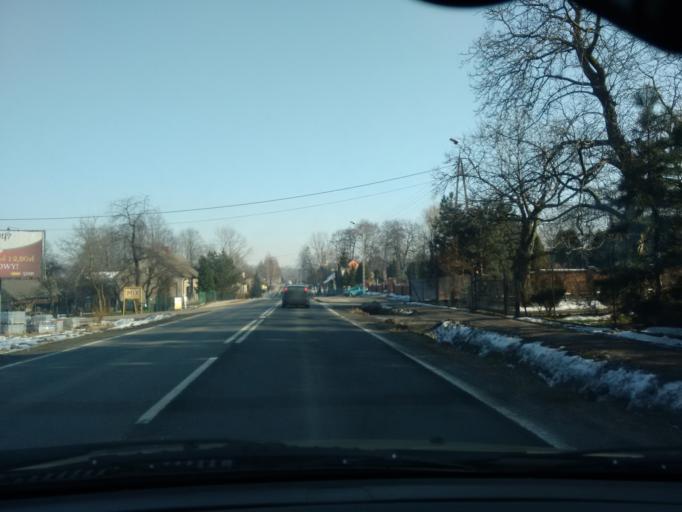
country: PL
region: Lesser Poland Voivodeship
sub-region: Powiat oswiecimski
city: Bulowice
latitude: 49.8778
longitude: 19.2757
